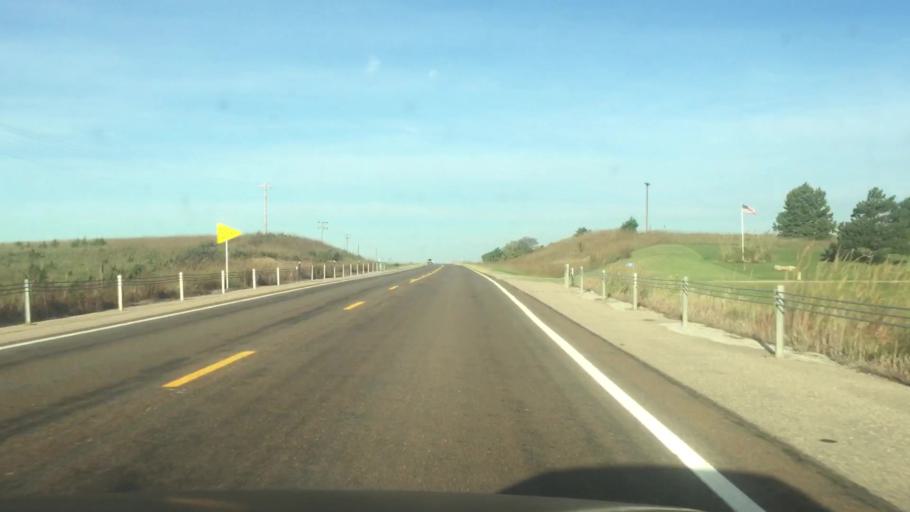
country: US
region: Nebraska
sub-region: Gage County
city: Wymore
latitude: 40.0458
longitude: -96.7619
